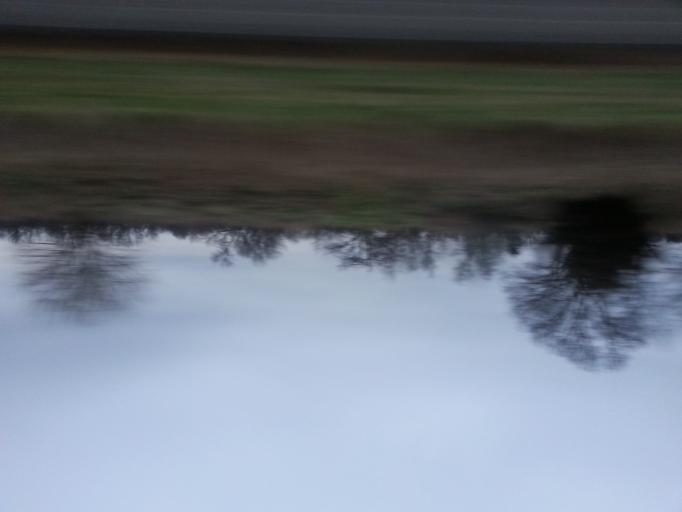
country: US
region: Iowa
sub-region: Linn County
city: Robins
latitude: 42.1166
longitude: -91.7114
